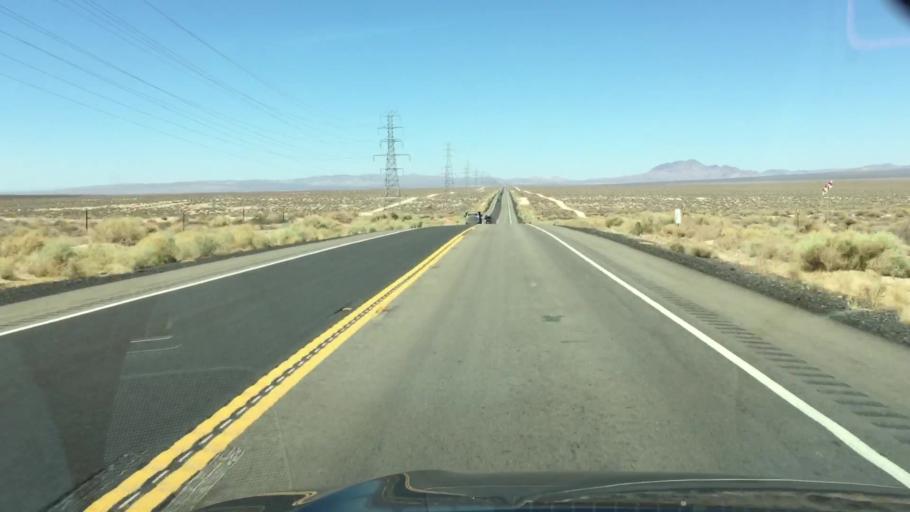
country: US
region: California
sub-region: Kern County
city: Boron
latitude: 35.1092
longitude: -117.5741
